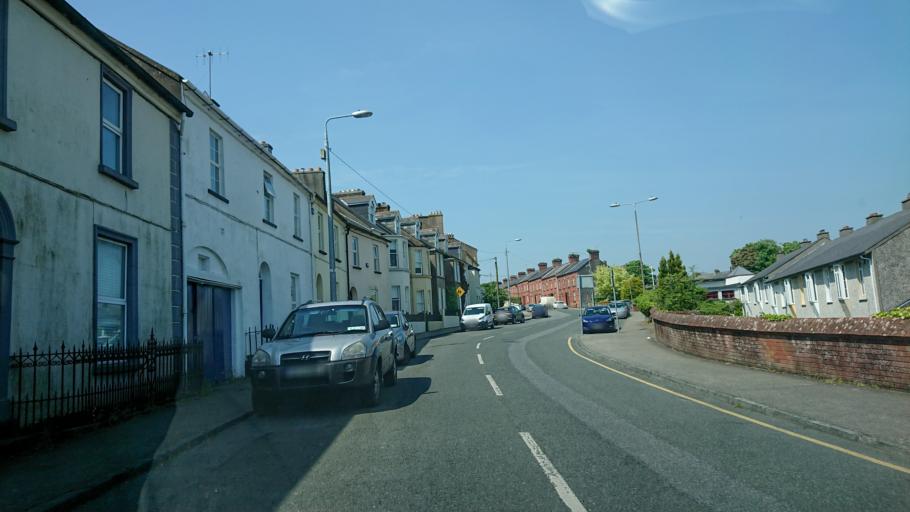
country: IE
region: Munster
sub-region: Waterford
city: Waterford
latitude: 52.2531
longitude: -7.1042
